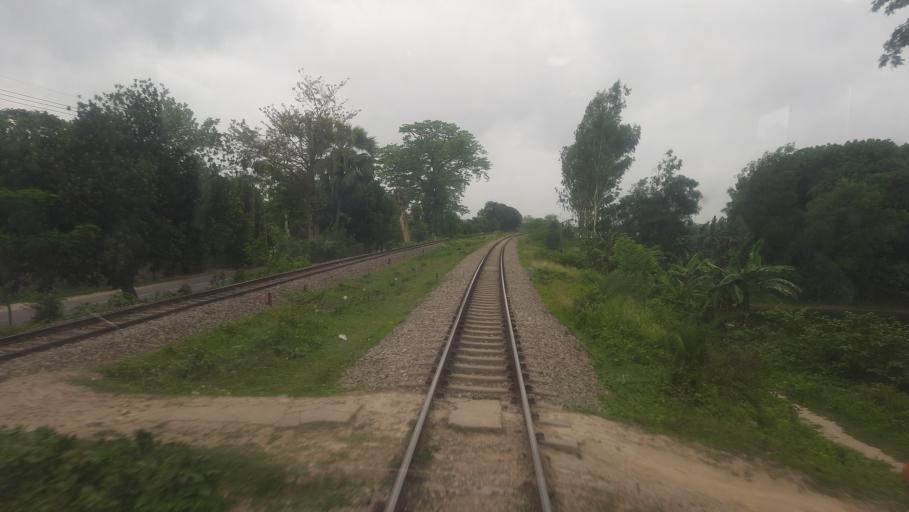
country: BD
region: Dhaka
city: Narsingdi
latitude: 23.9326
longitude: 90.7589
